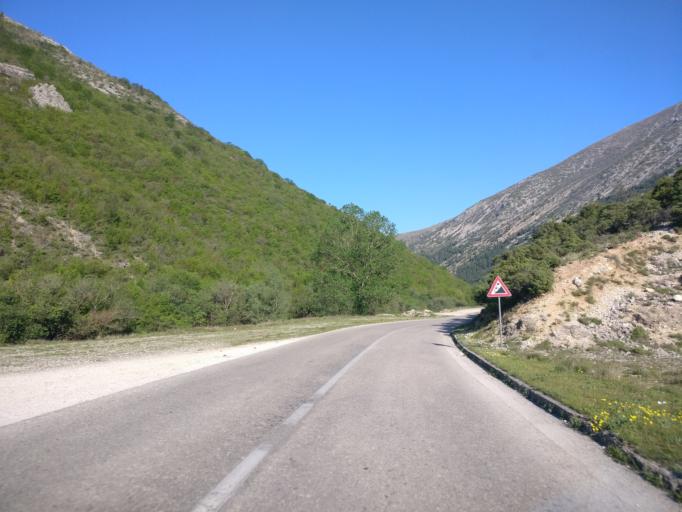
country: BA
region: Federation of Bosnia and Herzegovina
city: Stolac
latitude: 43.0916
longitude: 17.9961
